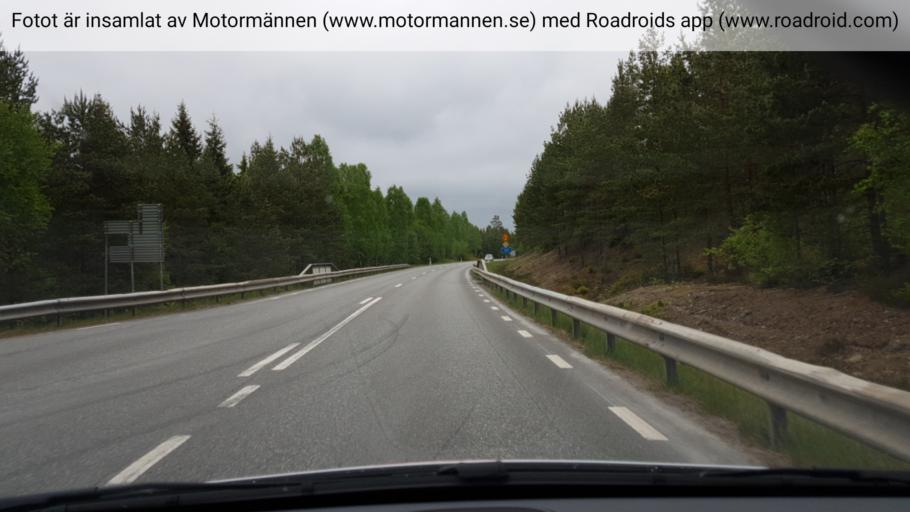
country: SE
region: Joenkoeping
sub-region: Mullsjo Kommun
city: Mullsjoe
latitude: 57.7764
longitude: 13.8347
